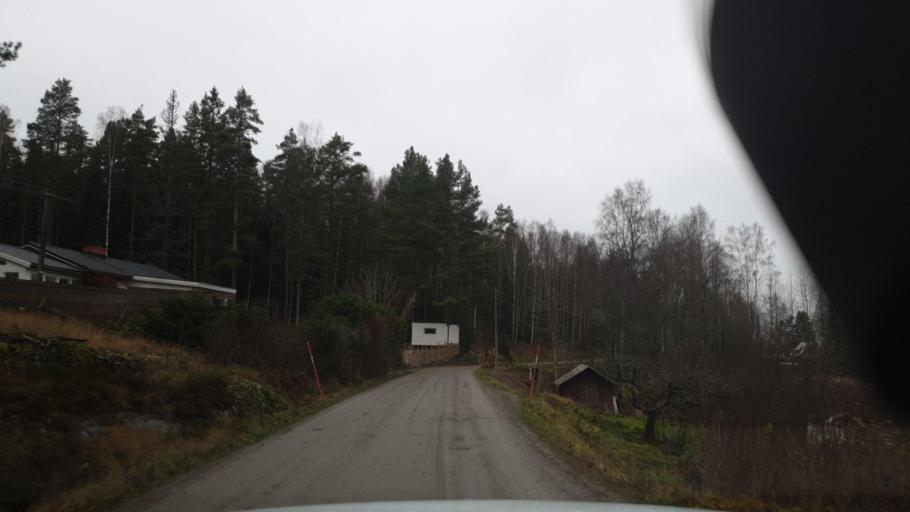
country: SE
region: Vaermland
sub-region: Eda Kommun
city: Amotfors
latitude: 59.7339
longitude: 12.2784
